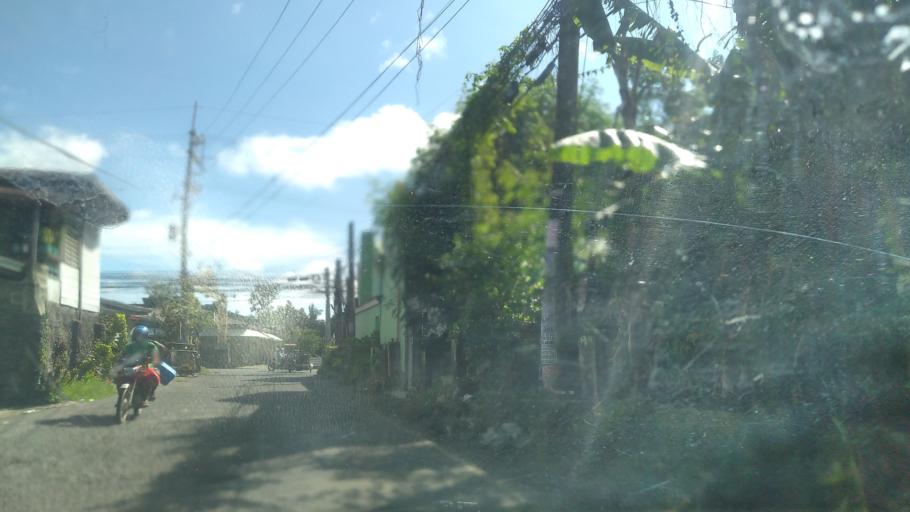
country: PH
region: Calabarzon
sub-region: Province of Quezon
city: Lucena
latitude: 13.9428
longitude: 121.6132
